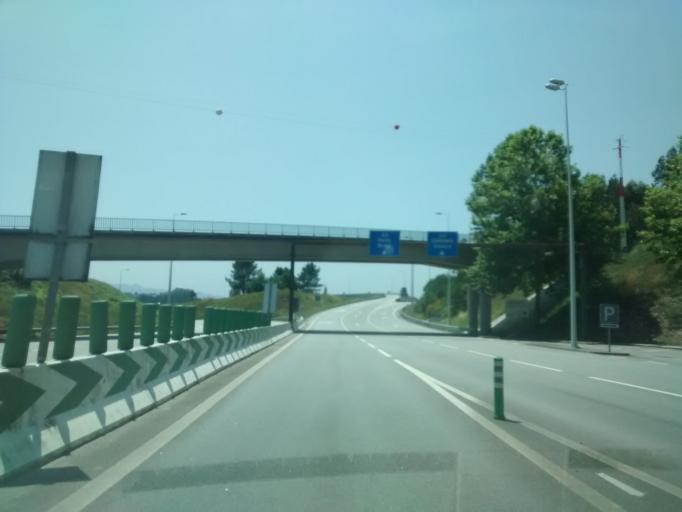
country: PT
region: Viana do Castelo
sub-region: Ponte de Lima
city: Ponte de Lima
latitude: 41.7793
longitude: -8.5577
